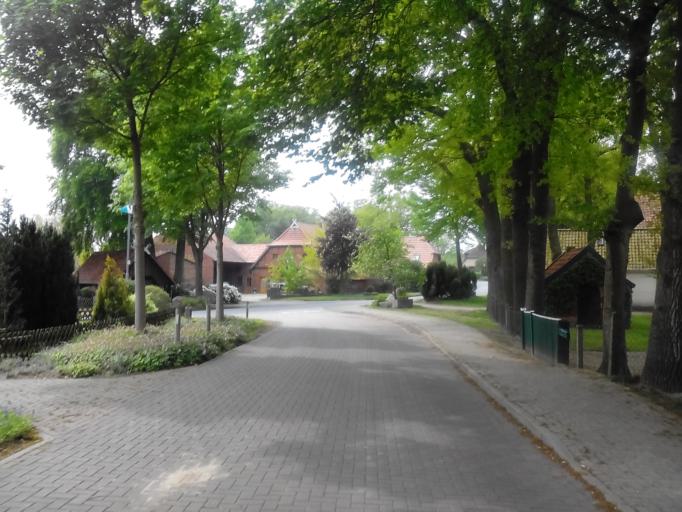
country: DE
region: Lower Saxony
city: Verden
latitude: 52.9212
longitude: 9.2636
